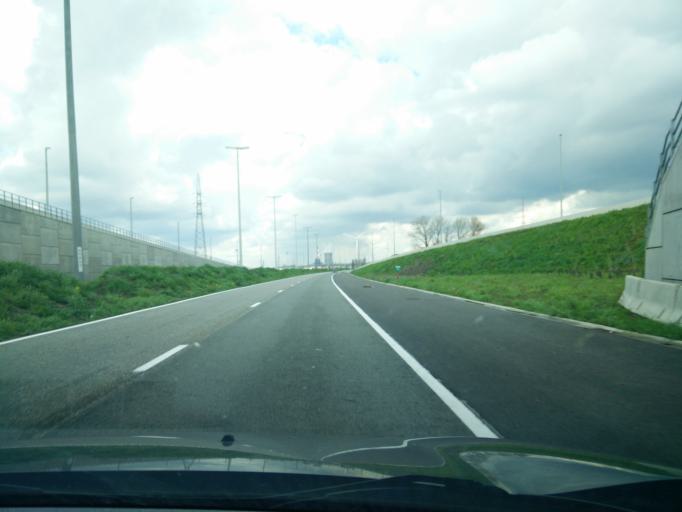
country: BE
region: Flanders
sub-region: Provincie Oost-Vlaanderen
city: Evergem
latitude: 51.1045
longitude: 3.7592
